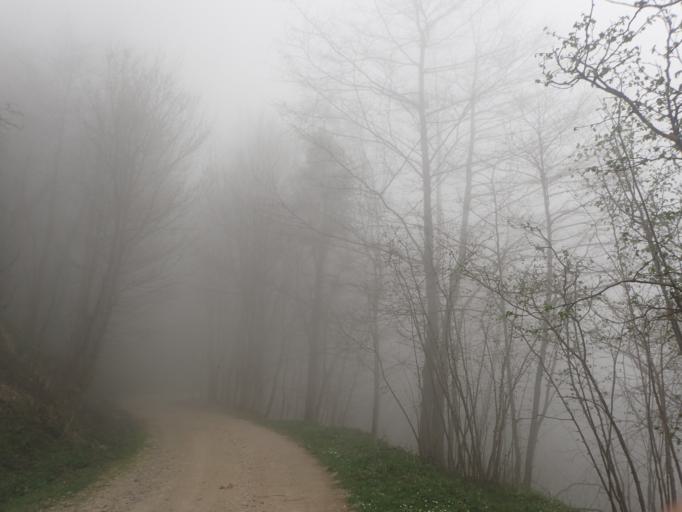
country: TR
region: Ordu
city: Korgan
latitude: 40.7846
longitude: 37.2714
